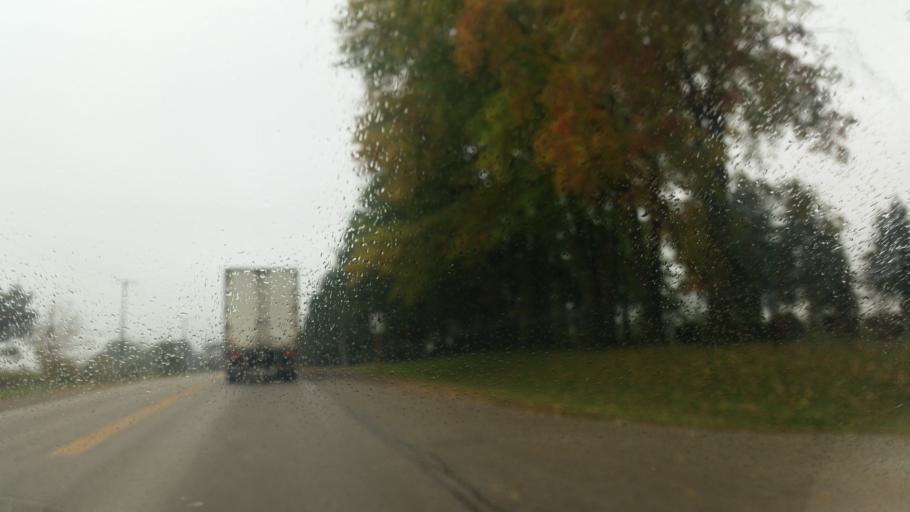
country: CA
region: Ontario
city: Waterloo
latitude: 43.6867
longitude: -80.4427
